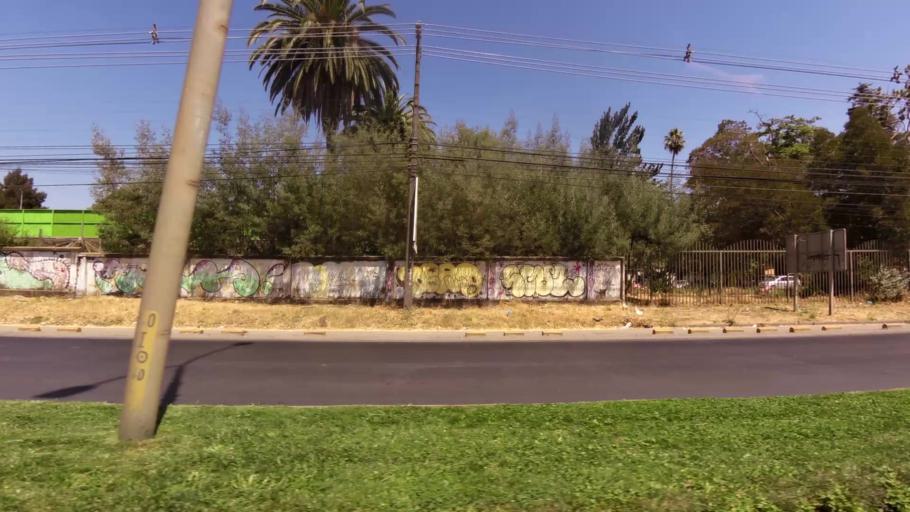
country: CL
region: Maule
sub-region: Provincia de Talca
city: Talca
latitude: -35.4390
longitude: -71.6144
